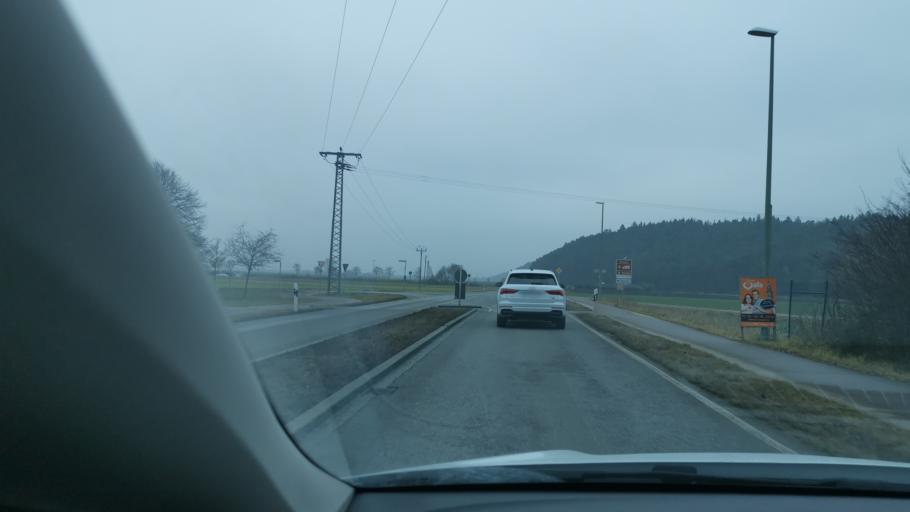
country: DE
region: Bavaria
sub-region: Swabia
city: Todtenweis
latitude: 48.5166
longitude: 10.9171
